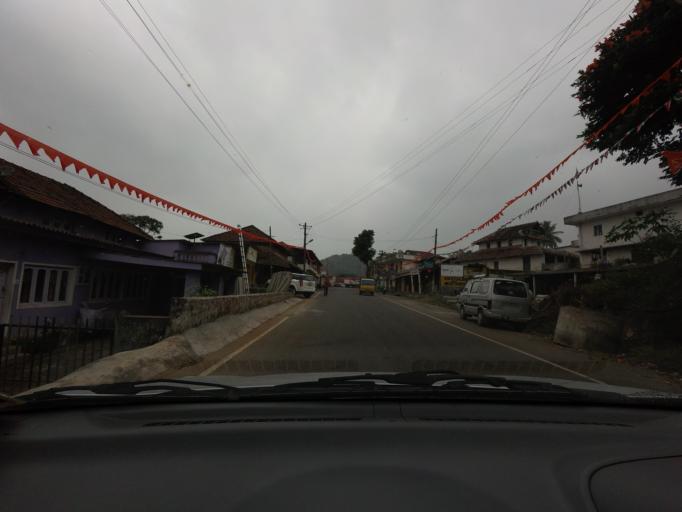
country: IN
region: Karnataka
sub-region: Hassan
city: Sakleshpur
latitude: 13.0040
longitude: 75.6979
